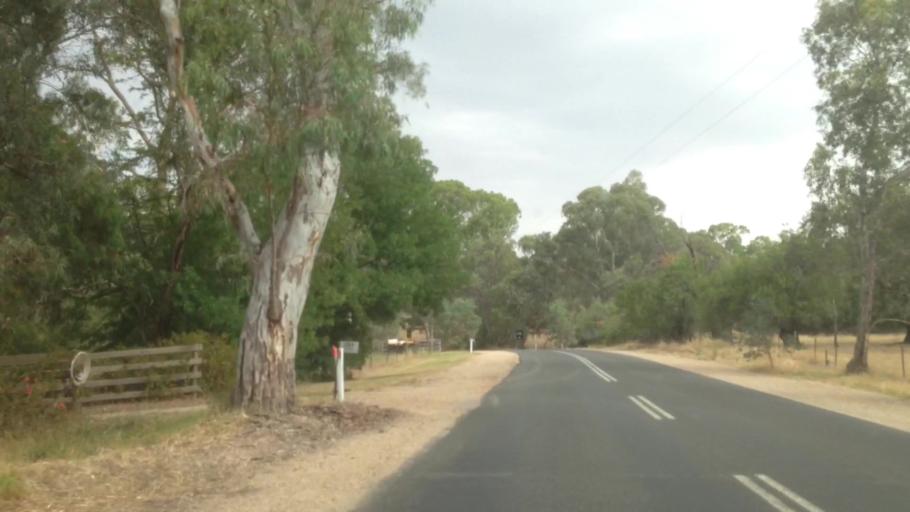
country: AU
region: South Australia
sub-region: Barossa
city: Williamstown
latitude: -34.6597
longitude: 138.8629
